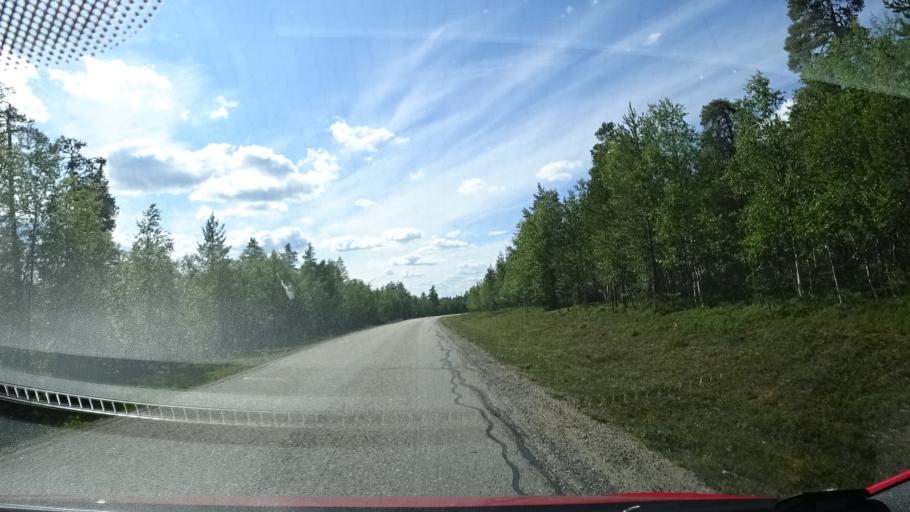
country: FI
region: Lapland
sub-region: Pohjois-Lappi
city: Inari
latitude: 68.4756
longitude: 26.0452
